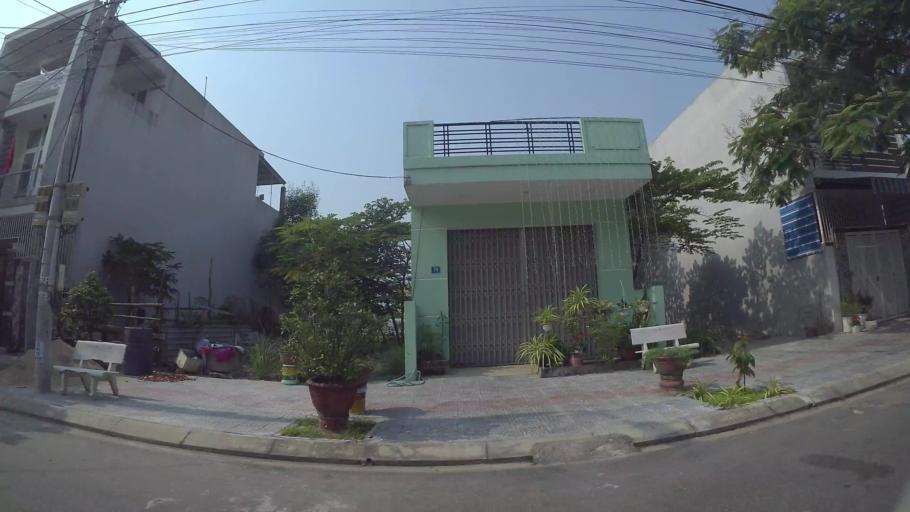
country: VN
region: Da Nang
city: Cam Le
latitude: 16.0033
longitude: 108.2230
